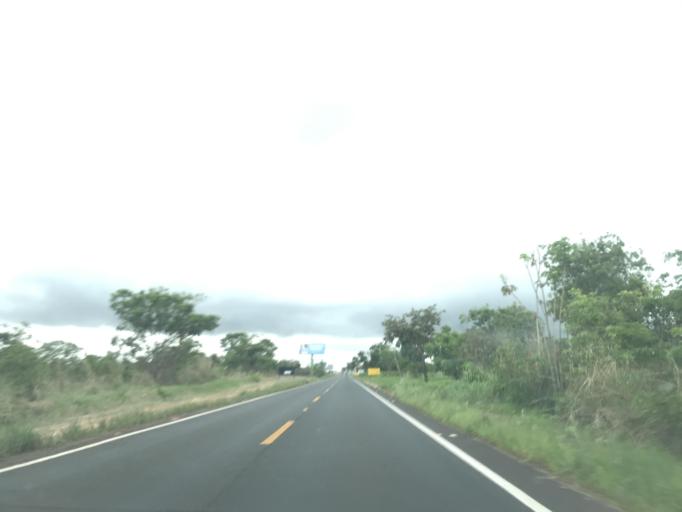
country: BR
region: Goias
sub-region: Caldas Novas
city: Caldas Novas
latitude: -17.6760
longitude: -48.7058
